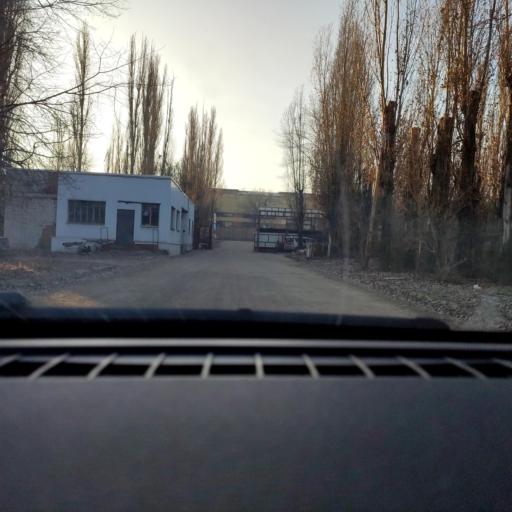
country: RU
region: Voronezj
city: Maslovka
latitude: 51.6025
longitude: 39.2619
